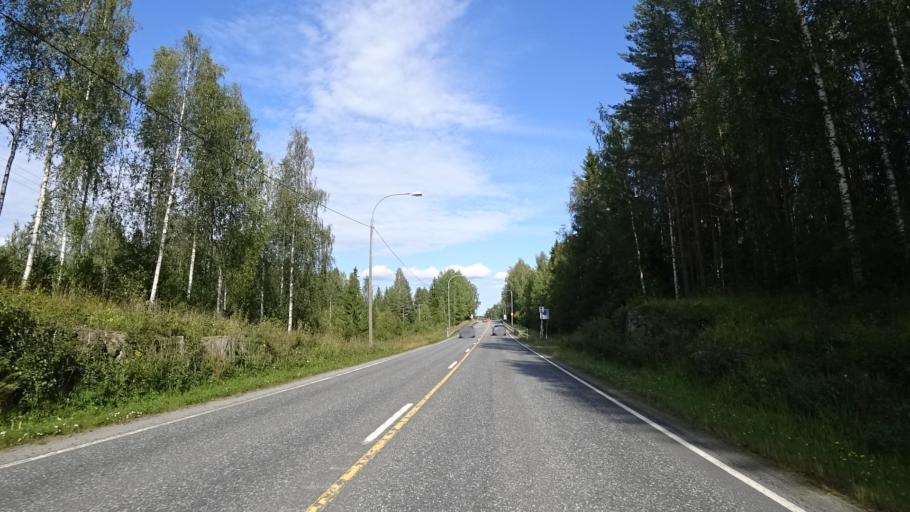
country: FI
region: North Karelia
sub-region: Joensuu
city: Eno
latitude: 62.7974
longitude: 30.1011
